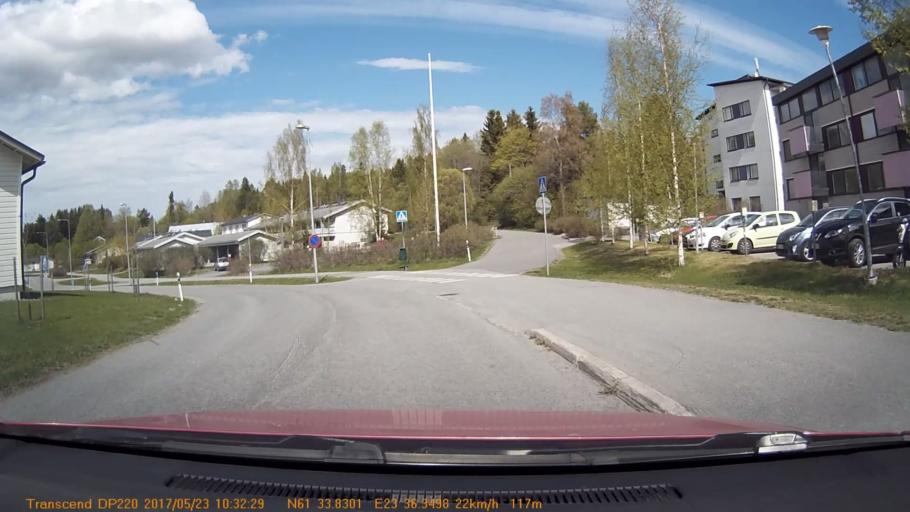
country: FI
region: Pirkanmaa
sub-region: Tampere
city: Yloejaervi
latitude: 61.5640
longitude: 23.6058
